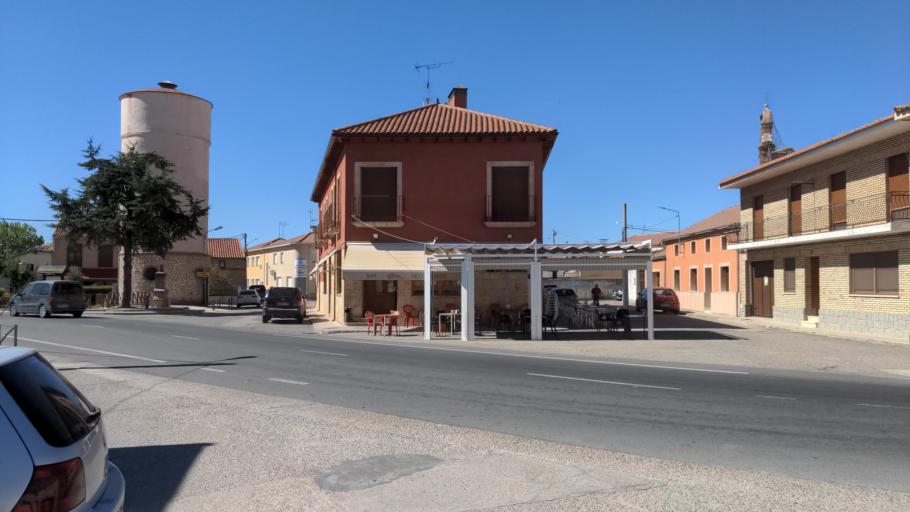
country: ES
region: Castille and Leon
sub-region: Provincia de Segovia
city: Chane
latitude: 41.3377
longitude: -4.4288
